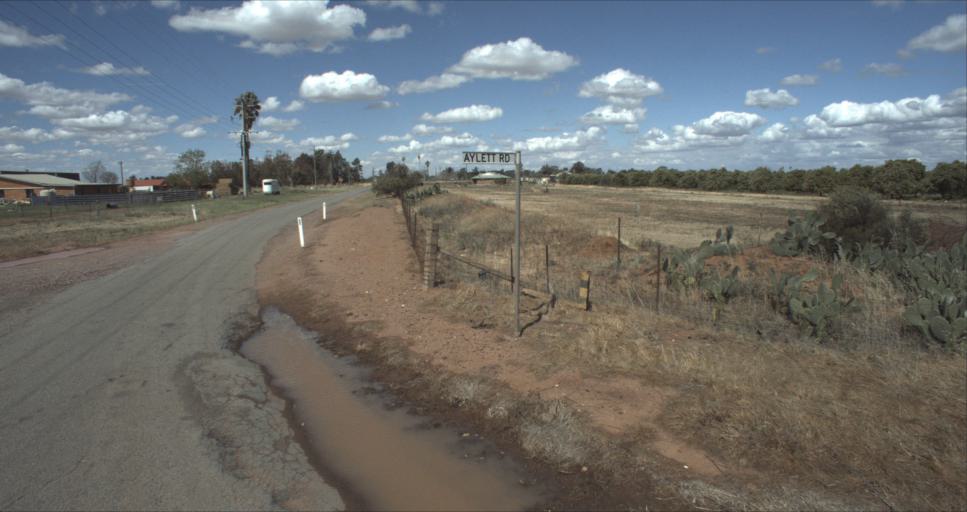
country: AU
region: New South Wales
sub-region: Leeton
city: Leeton
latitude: -34.5127
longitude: 146.2418
